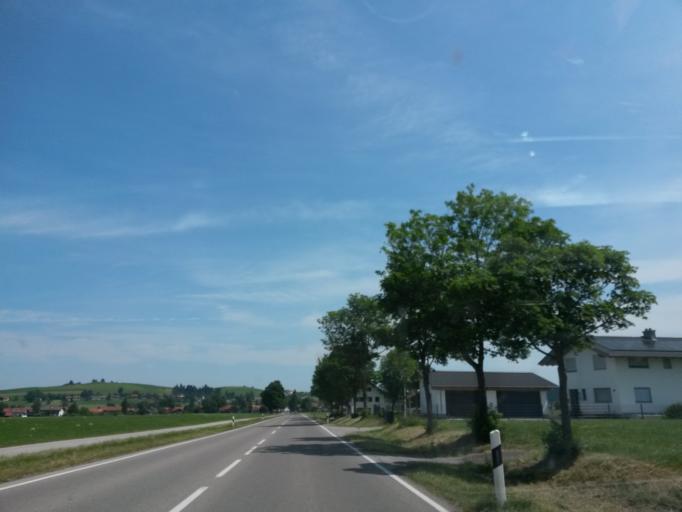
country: DE
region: Bavaria
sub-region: Swabia
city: Halblech
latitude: 47.6346
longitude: 10.8226
